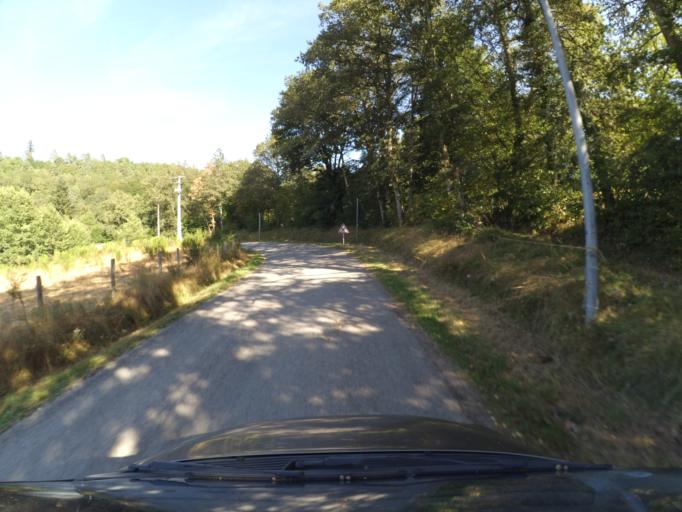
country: FR
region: Limousin
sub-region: Departement de la Correze
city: Bugeat
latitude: 45.6839
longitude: 1.8997
